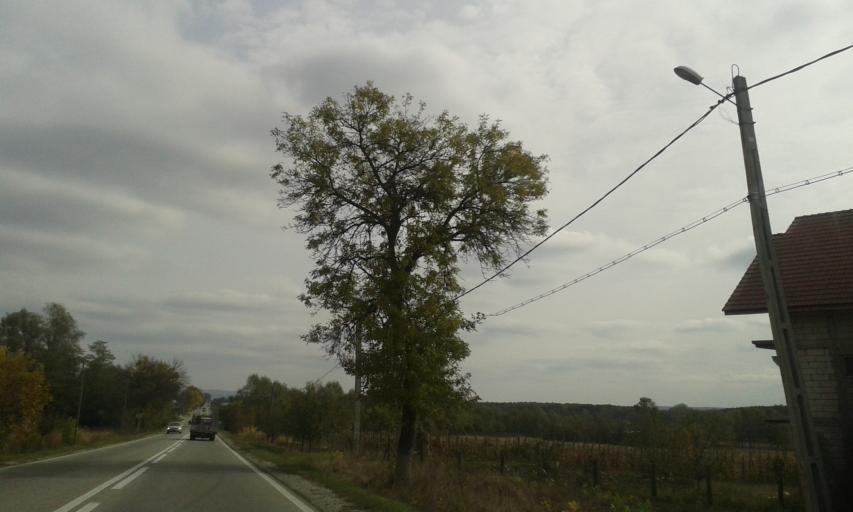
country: RO
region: Gorj
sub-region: Comuna Scoarta
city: Scoarta
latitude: 45.0310
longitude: 23.4164
